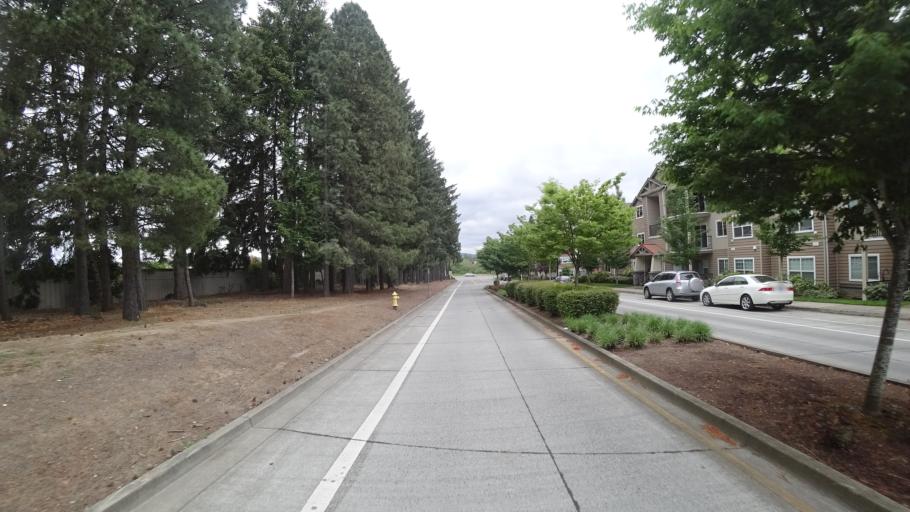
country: US
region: Oregon
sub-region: Washington County
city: Rockcreek
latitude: 45.5233
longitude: -122.8692
